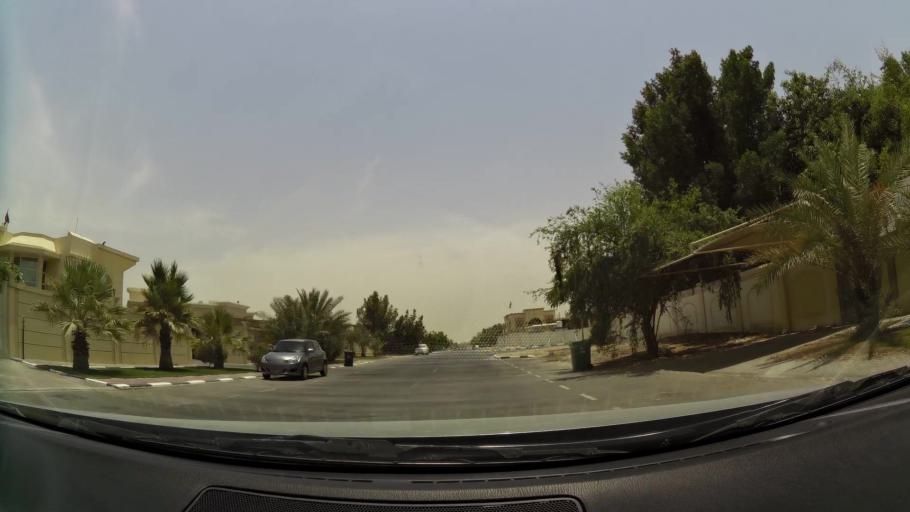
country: AE
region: Ash Shariqah
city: Sharjah
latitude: 25.2078
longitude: 55.3948
